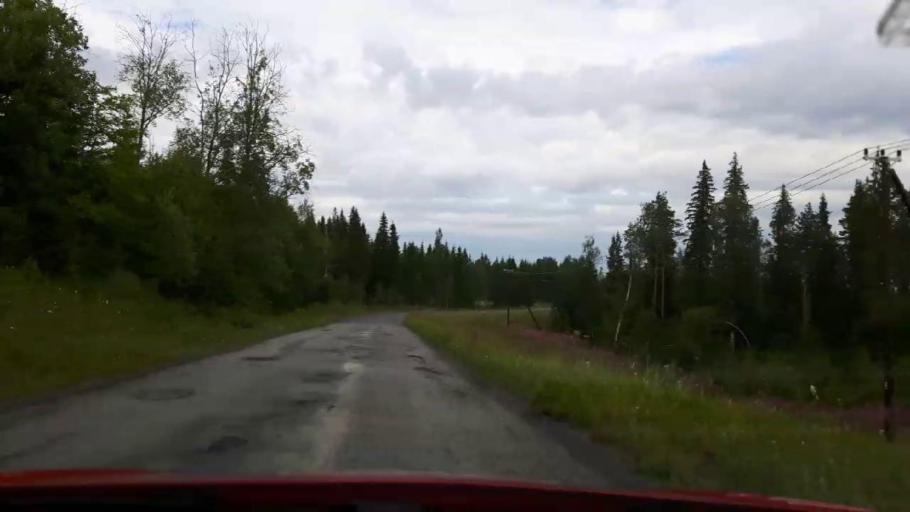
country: SE
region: Jaemtland
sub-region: Stroemsunds Kommun
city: Stroemsund
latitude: 63.5315
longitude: 15.3551
